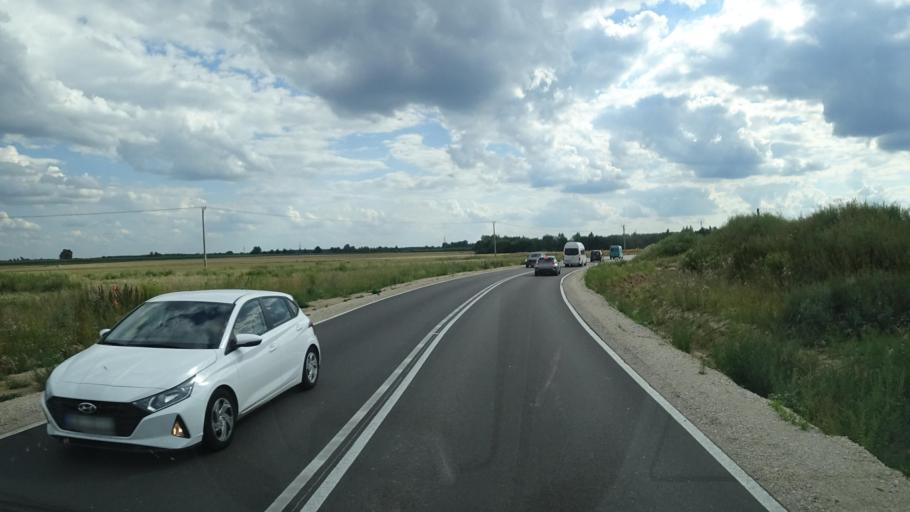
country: PL
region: Masovian Voivodeship
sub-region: Powiat ostrowski
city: Ostrow Mazowiecka
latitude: 52.8199
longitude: 21.9230
